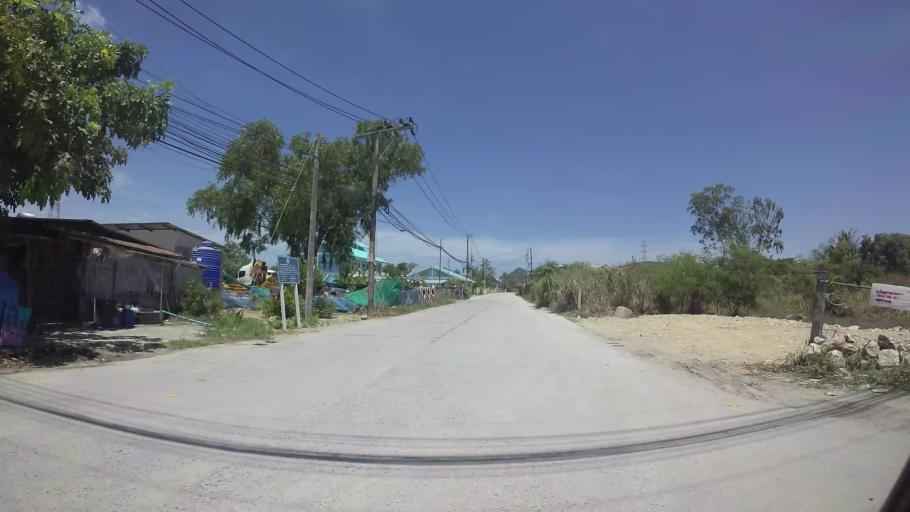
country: TH
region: Chon Buri
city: Si Racha
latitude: 13.1299
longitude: 100.9531
